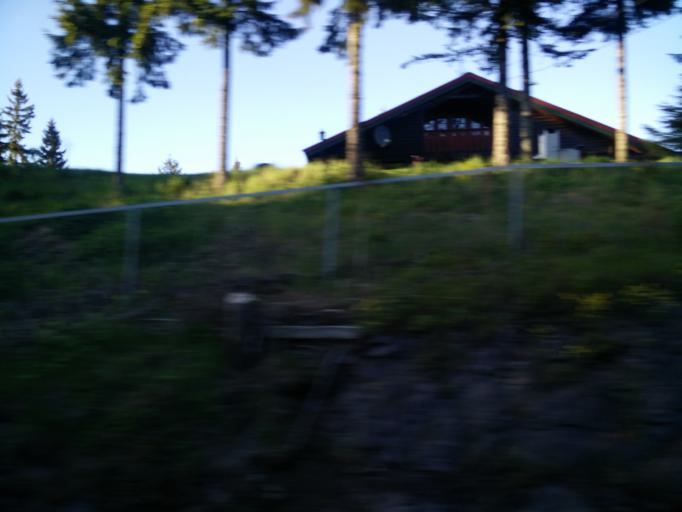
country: NO
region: Akershus
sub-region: Baerum
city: Skui
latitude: 59.9545
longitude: 10.3752
